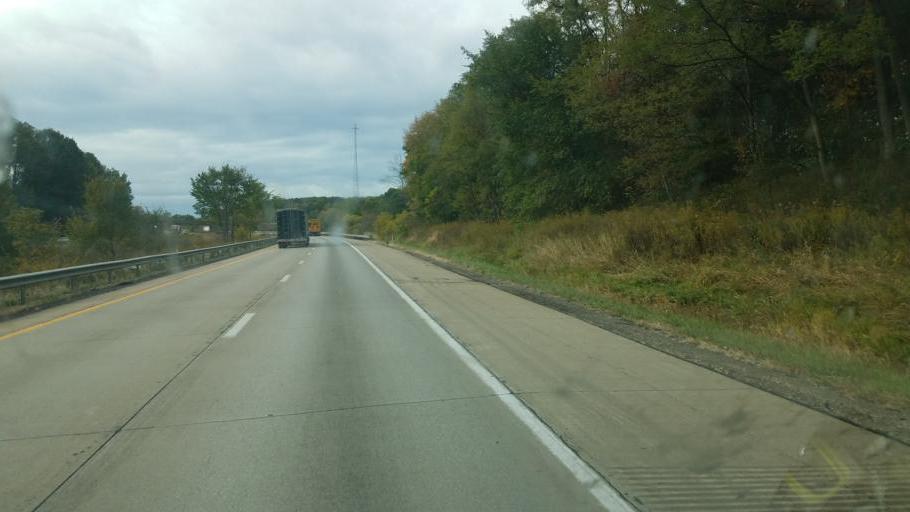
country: US
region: Pennsylvania
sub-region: Lawrence County
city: New Wilmington
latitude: 41.1832
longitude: -80.3217
